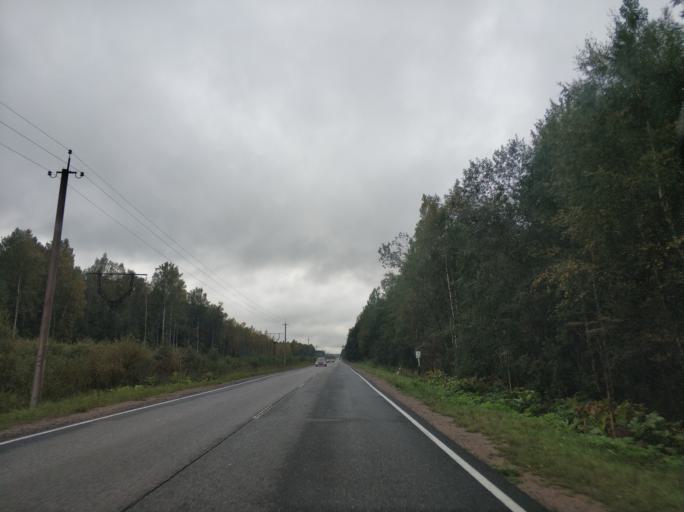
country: RU
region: Leningrad
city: Borisova Griva
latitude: 60.1081
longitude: 30.9599
